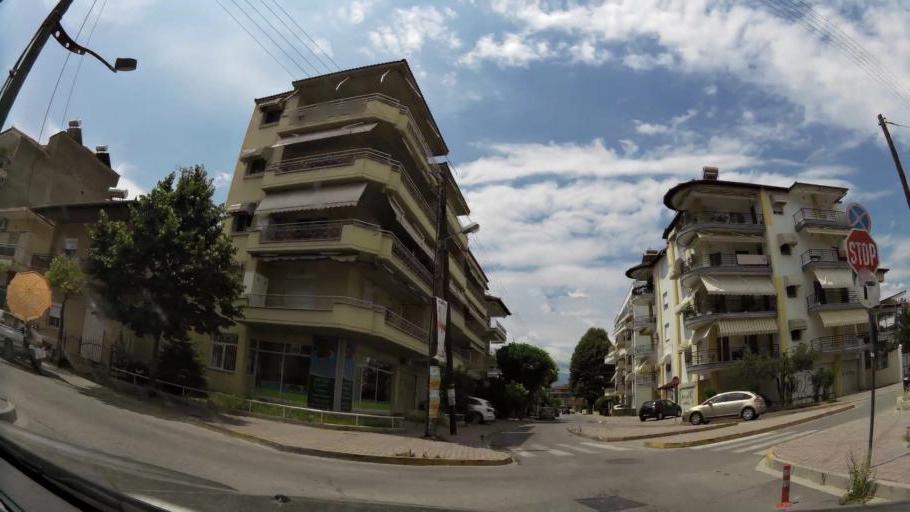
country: GR
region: Central Macedonia
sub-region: Nomos Pierias
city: Katerini
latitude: 40.2684
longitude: 22.5133
